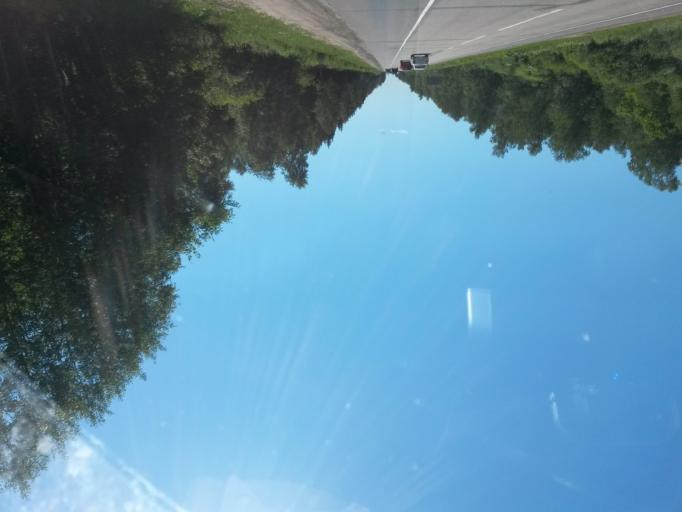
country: RU
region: Moskovskaya
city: Proletarskiy
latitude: 55.0586
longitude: 37.4346
